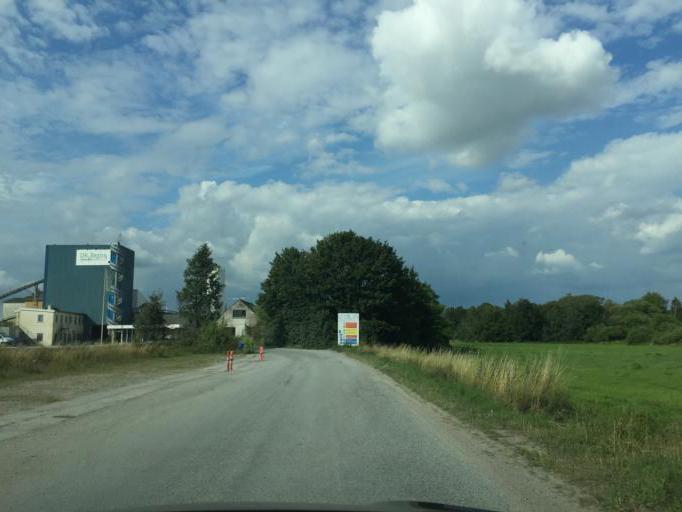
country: DK
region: South Denmark
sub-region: Kerteminde Kommune
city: Langeskov
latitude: 55.3676
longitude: 10.5807
